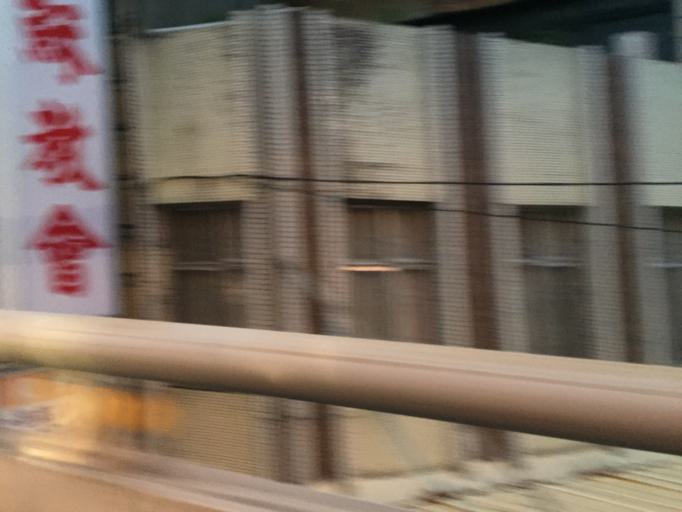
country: TW
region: Taiwan
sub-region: Yilan
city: Yilan
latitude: 24.7573
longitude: 121.7455
